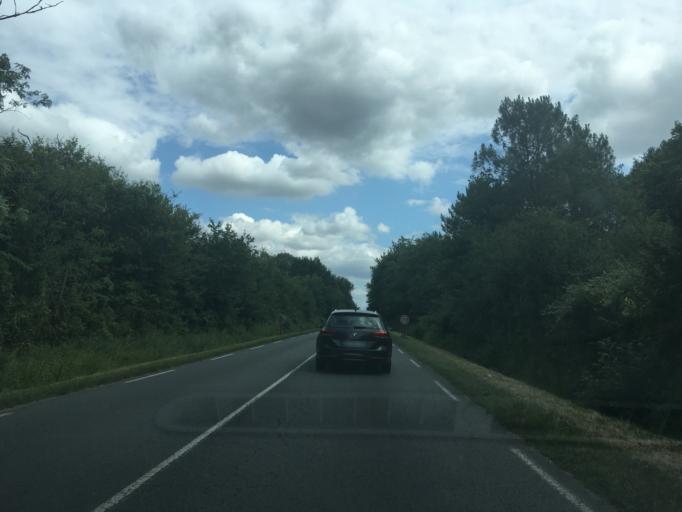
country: FR
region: Aquitaine
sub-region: Departement de la Gironde
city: Le Taillan-Medoc
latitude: 44.9209
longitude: -0.6733
